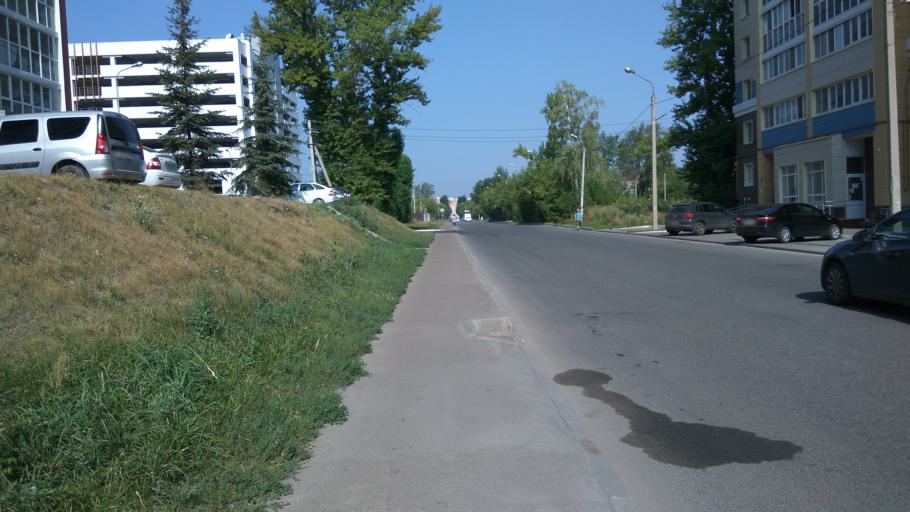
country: RU
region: Tatarstan
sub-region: Gorod Kazan'
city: Kazan
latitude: 55.7689
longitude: 49.1525
